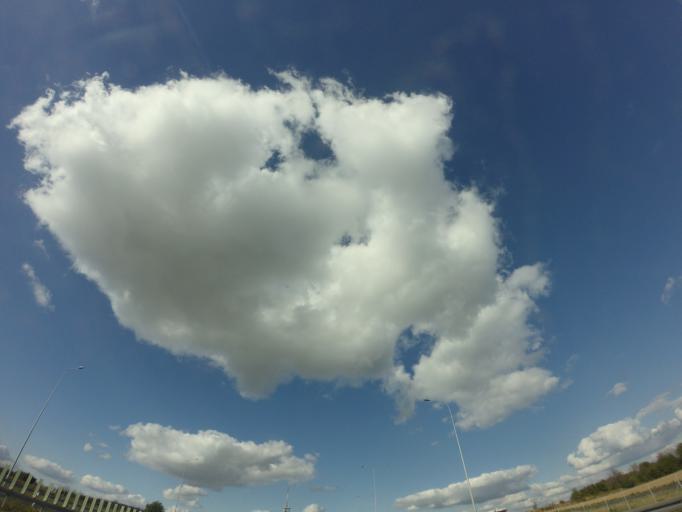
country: PL
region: Lower Silesian Voivodeship
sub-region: Powiat trzebnicki
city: Trzebnica
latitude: 51.2996
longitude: 17.0363
